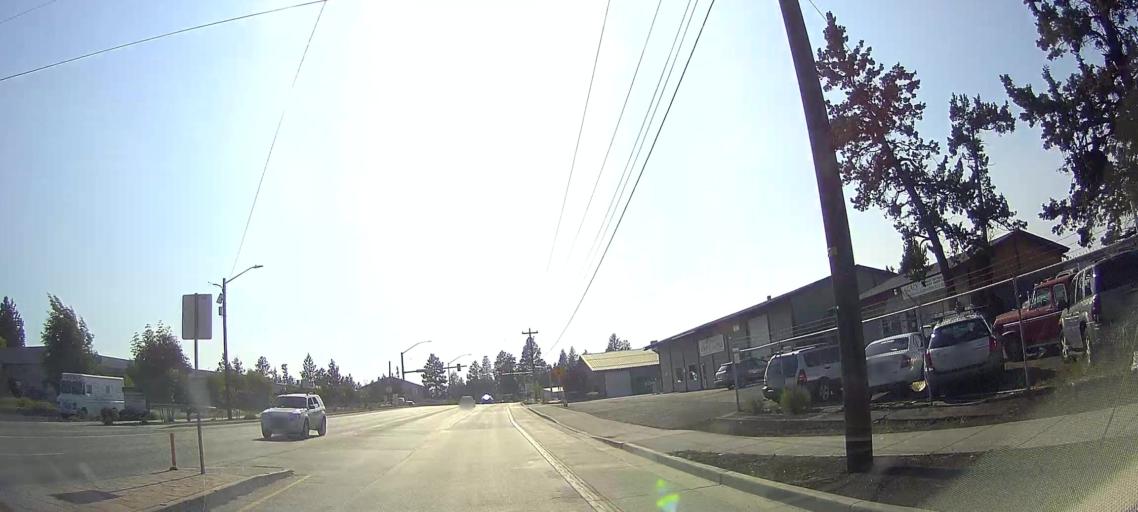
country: US
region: Oregon
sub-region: Deschutes County
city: Bend
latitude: 44.0371
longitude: -121.2896
